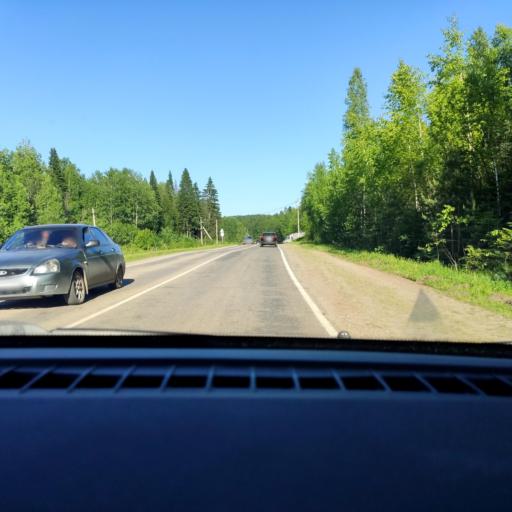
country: RU
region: Perm
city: Overyata
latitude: 58.1257
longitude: 55.8607
